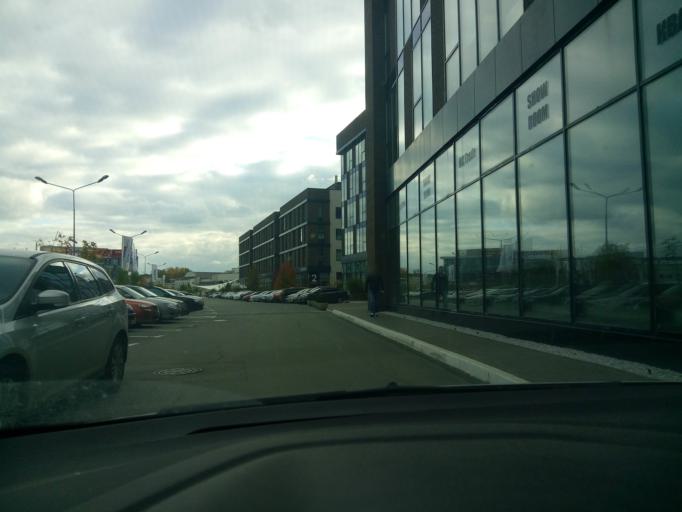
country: RU
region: Sverdlovsk
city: Yekaterinburg
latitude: 56.8223
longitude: 60.6510
